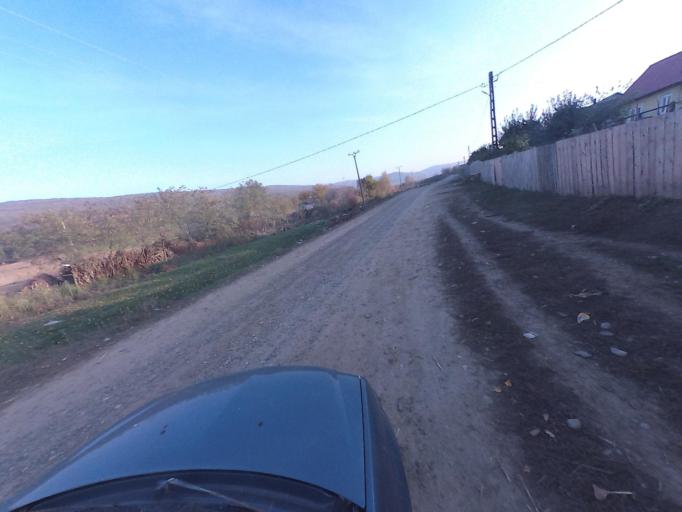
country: RO
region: Vaslui
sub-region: Comuna Bacesti
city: Bacesti
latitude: 46.8101
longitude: 27.2362
